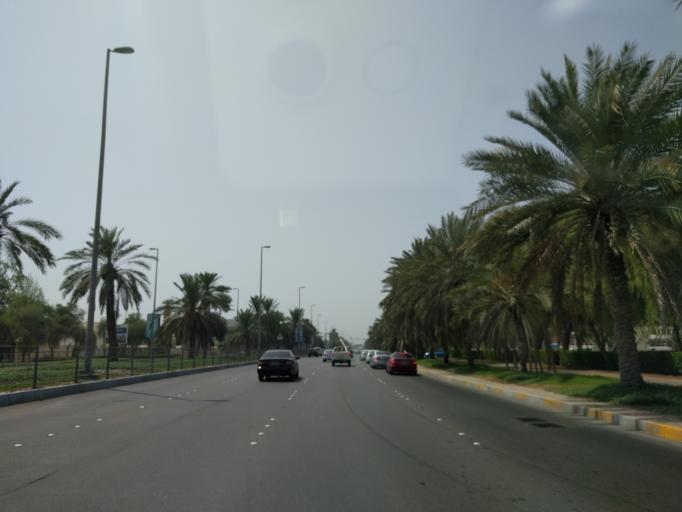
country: AE
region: Abu Dhabi
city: Abu Dhabi
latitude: 24.4436
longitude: 54.4041
